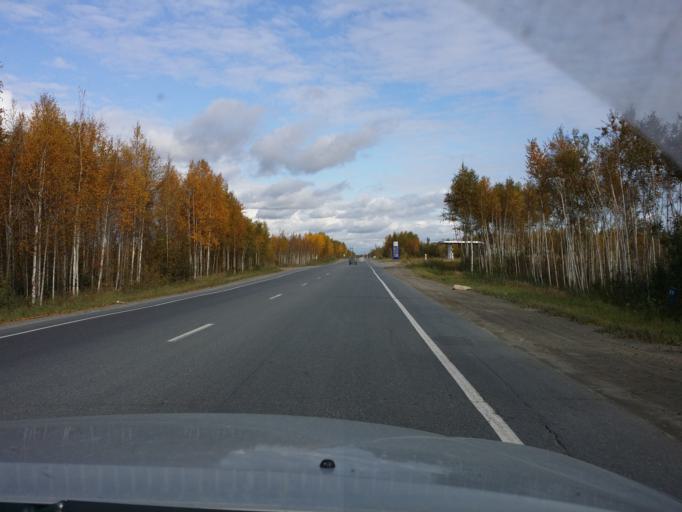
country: RU
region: Khanty-Mansiyskiy Avtonomnyy Okrug
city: Megion
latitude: 61.0677
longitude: 76.1157
